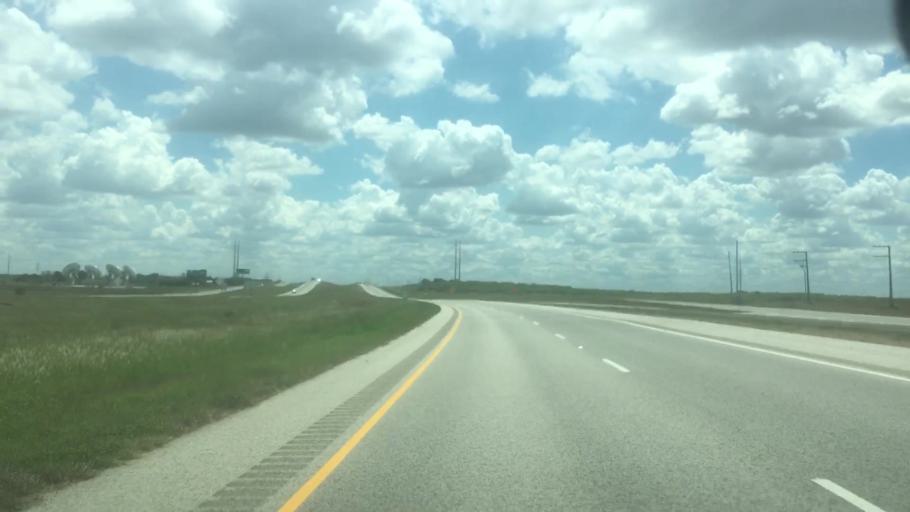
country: US
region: Texas
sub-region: Caldwell County
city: Uhland
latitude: 30.0156
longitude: -97.6883
